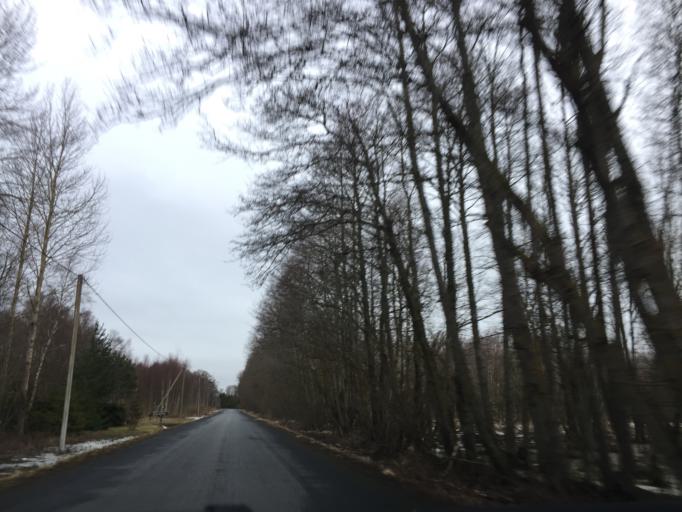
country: EE
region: Laeaene
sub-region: Haapsalu linn
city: Haapsalu
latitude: 58.7976
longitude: 23.4921
